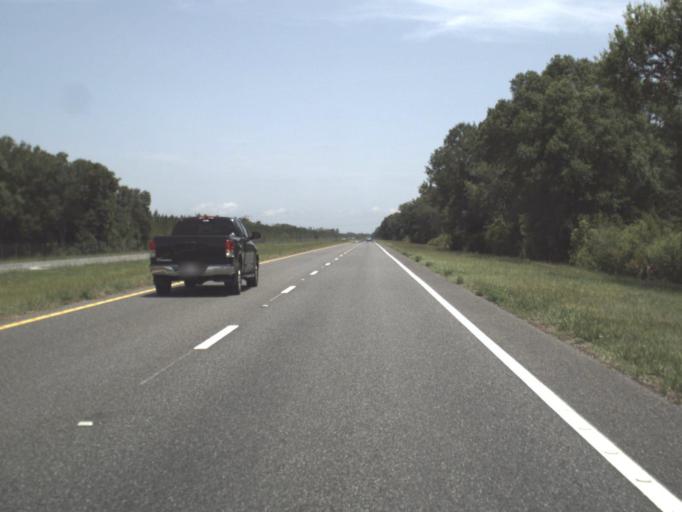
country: US
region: Florida
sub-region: Taylor County
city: Steinhatchee
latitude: 29.7890
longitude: -83.3321
